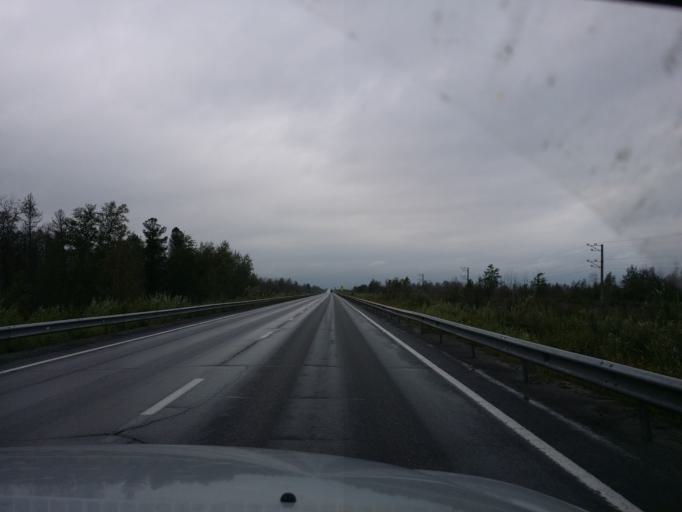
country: RU
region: Khanty-Mansiyskiy Avtonomnyy Okrug
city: Lokosovo
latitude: 61.4535
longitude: 74.6927
